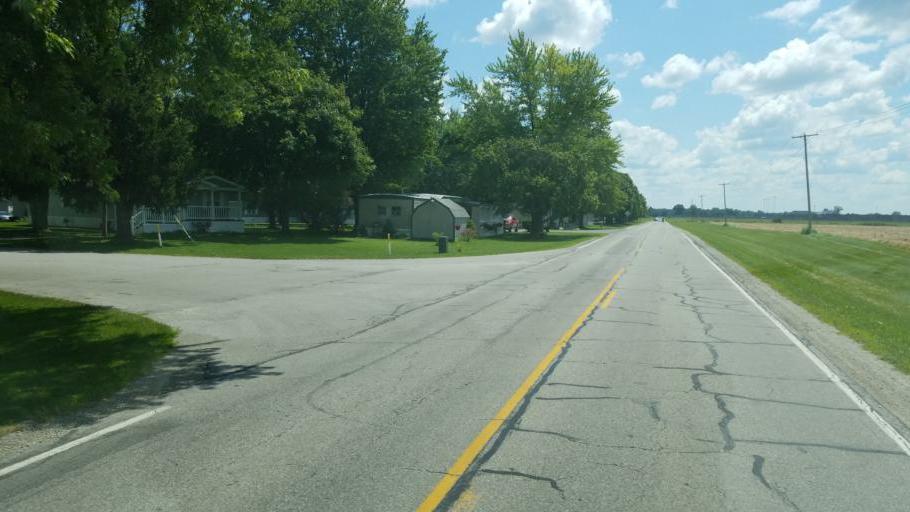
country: US
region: Ohio
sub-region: Marion County
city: Marion
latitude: 40.6289
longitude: -83.1014
